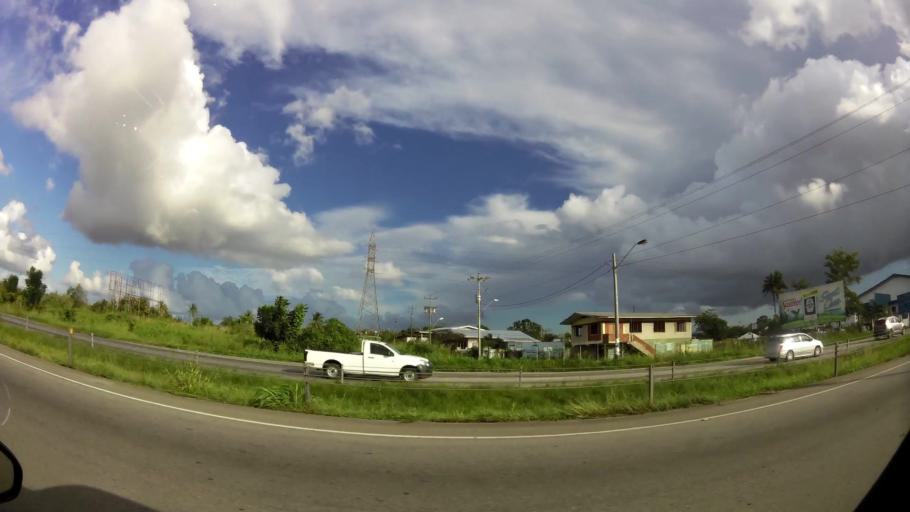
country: TT
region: Chaguanas
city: Chaguanas
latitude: 10.4730
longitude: -61.4051
